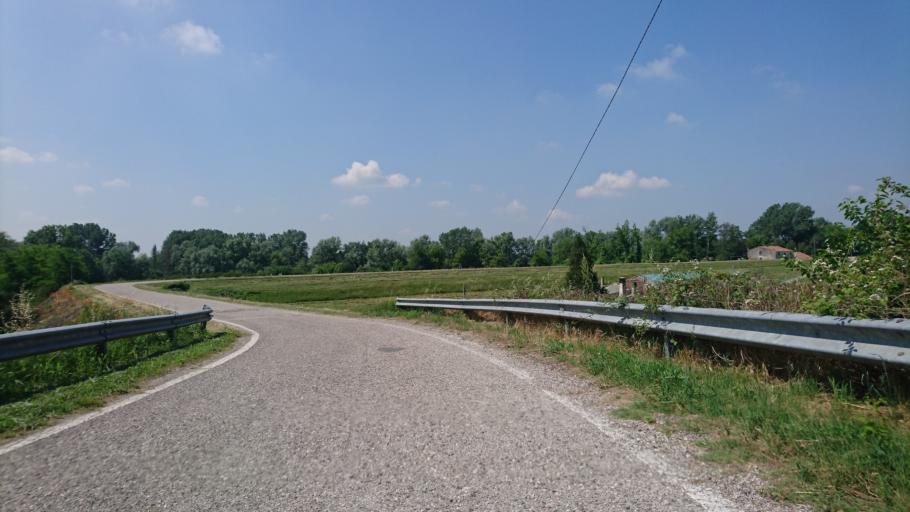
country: IT
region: Lombardy
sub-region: Provincia di Mantova
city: Sustinente
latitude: 45.0771
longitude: 10.9769
